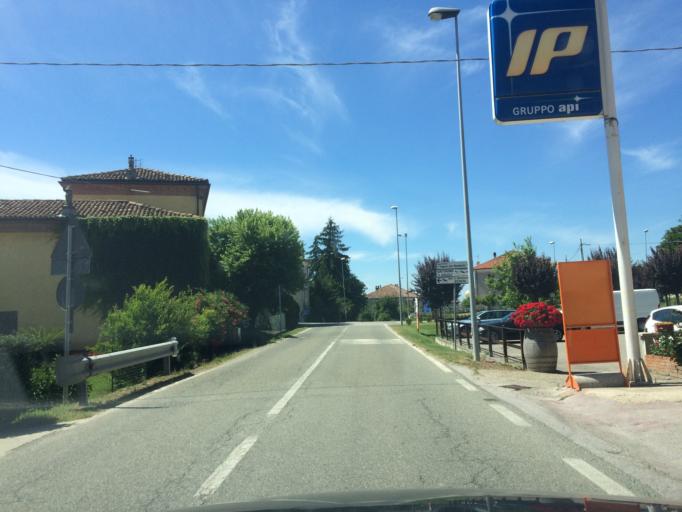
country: IT
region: Piedmont
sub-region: Provincia di Asti
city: Castel Boglione
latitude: 44.7428
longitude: 8.3867
